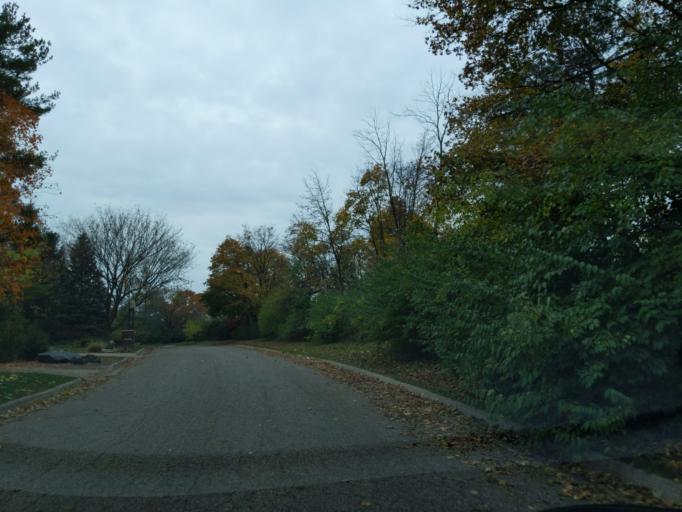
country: US
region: Michigan
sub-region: Ingham County
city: Edgemont Park
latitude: 42.7185
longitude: -84.5866
